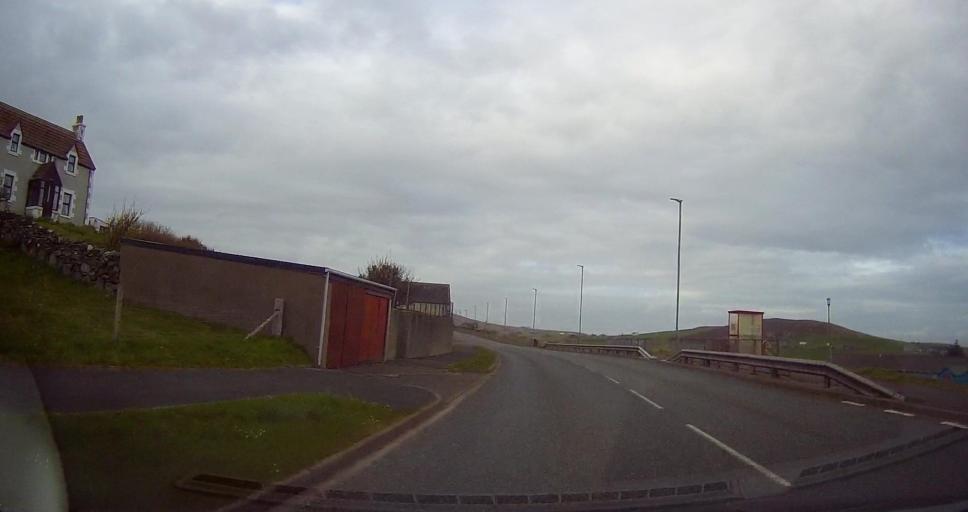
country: GB
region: Scotland
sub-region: Shetland Islands
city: Sandwick
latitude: 60.0453
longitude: -1.2280
